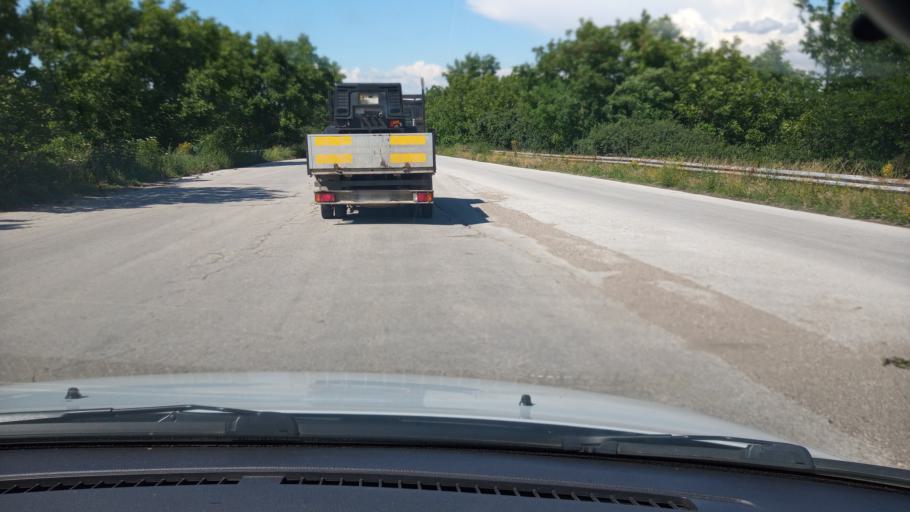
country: BG
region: Pleven
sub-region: Obshtina Dolna Mitropoliya
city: Dolna Mitropoliya
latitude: 43.4407
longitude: 24.5264
